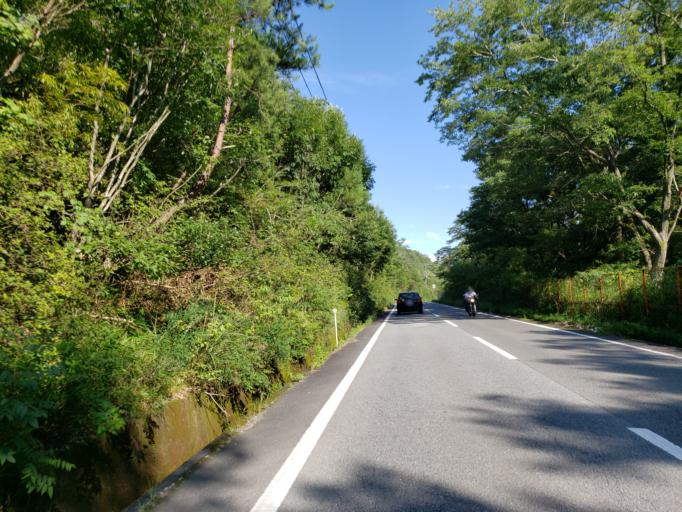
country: JP
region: Hyogo
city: Kakogawacho-honmachi
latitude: 34.8613
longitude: 134.8006
